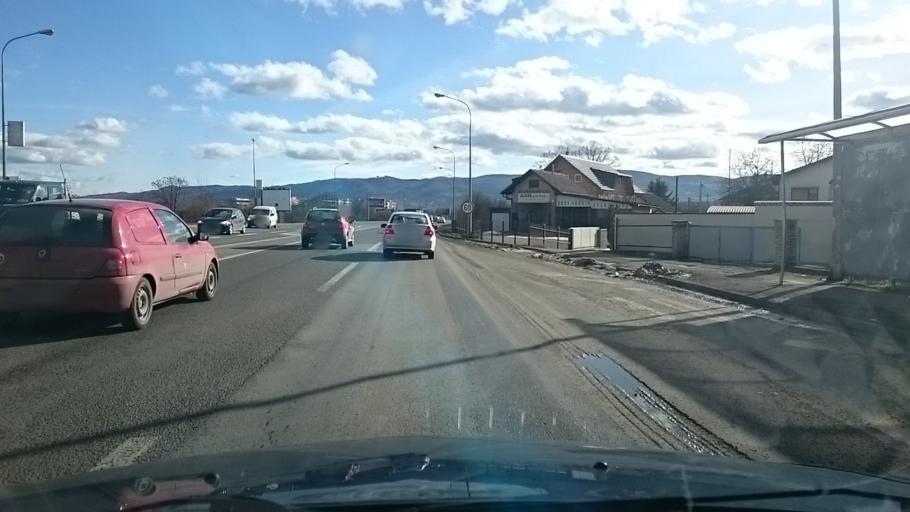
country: BA
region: Republika Srpska
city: Banja Luka
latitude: 44.7962
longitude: 17.1988
